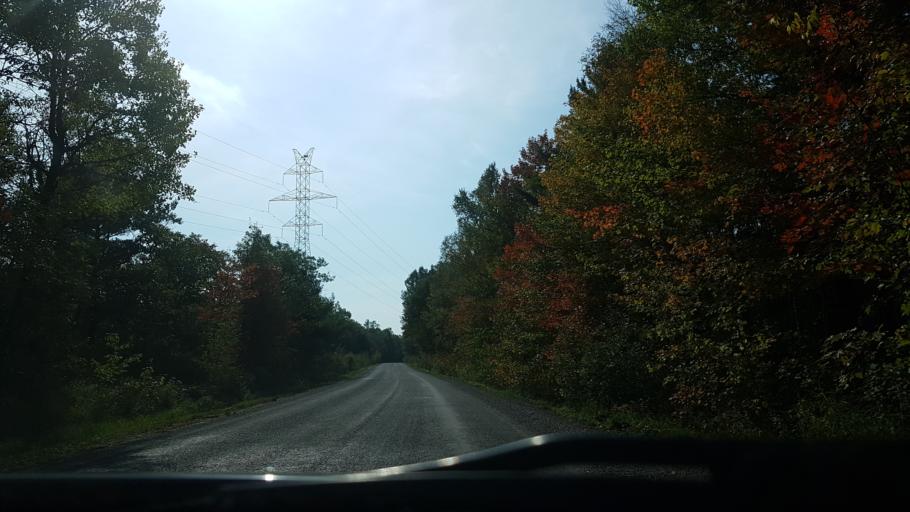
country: CA
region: Ontario
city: Gravenhurst
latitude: 44.8104
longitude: -79.2122
